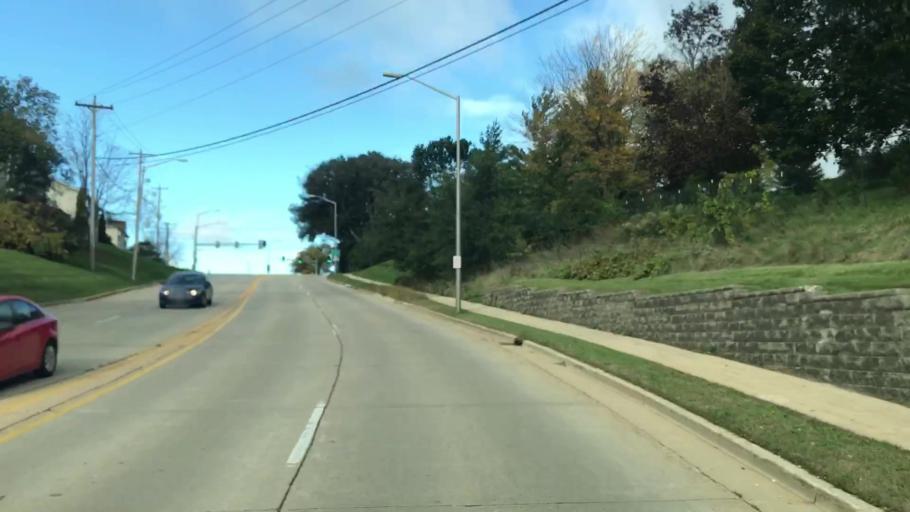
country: US
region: Wisconsin
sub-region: Waukesha County
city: Waukesha
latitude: 43.0233
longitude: -88.2238
